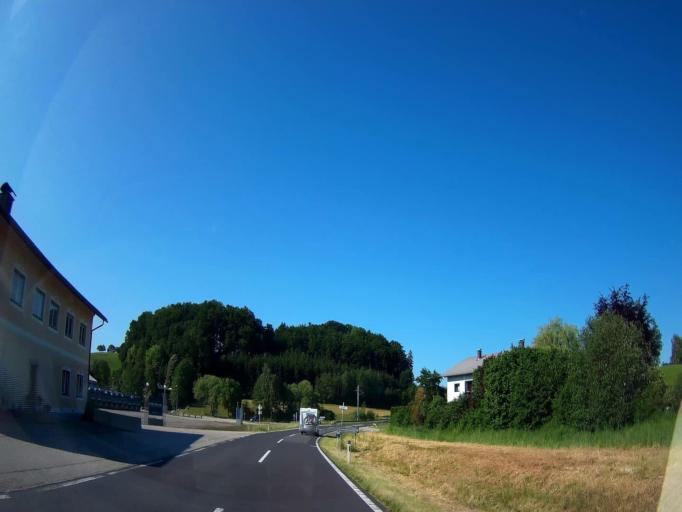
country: AT
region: Salzburg
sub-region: Politischer Bezirk Salzburg-Umgebung
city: Dorfbeuern
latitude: 48.1248
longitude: 13.0079
